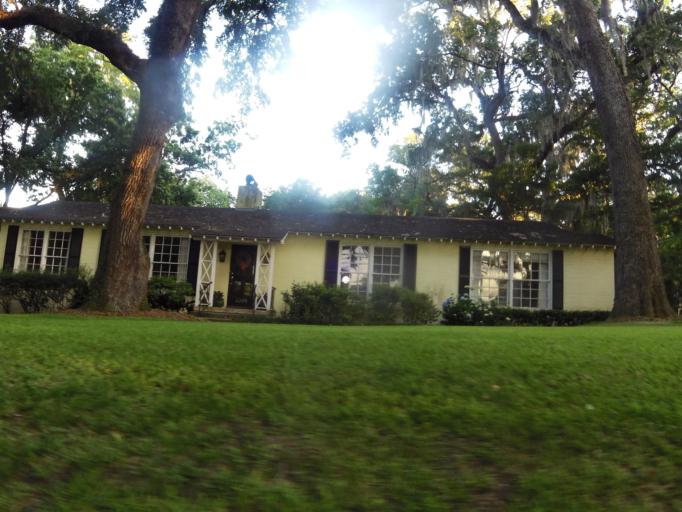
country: US
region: Florida
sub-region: Duval County
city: Jacksonville
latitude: 30.2729
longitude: -81.7122
